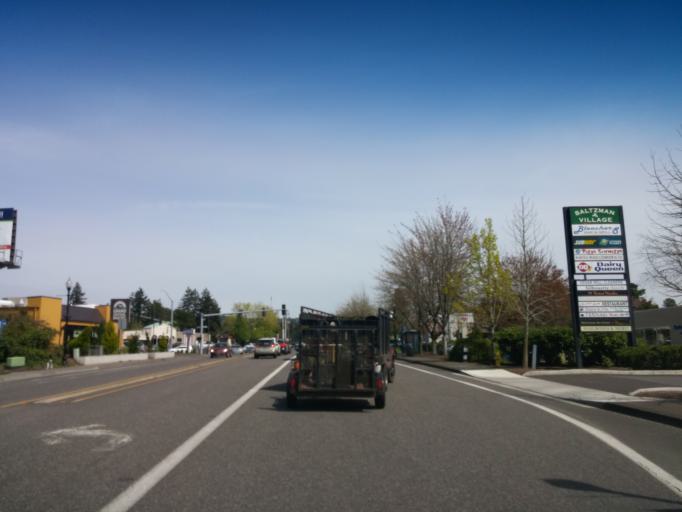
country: US
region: Oregon
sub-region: Washington County
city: Cedar Mill
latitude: 45.5251
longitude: -122.8075
